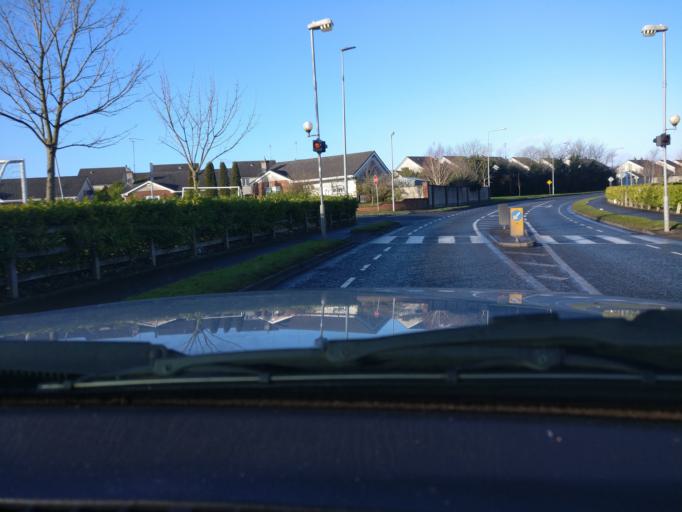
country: IE
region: Leinster
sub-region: An Iarmhi
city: An Muileann gCearr
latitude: 53.5190
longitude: -7.3712
